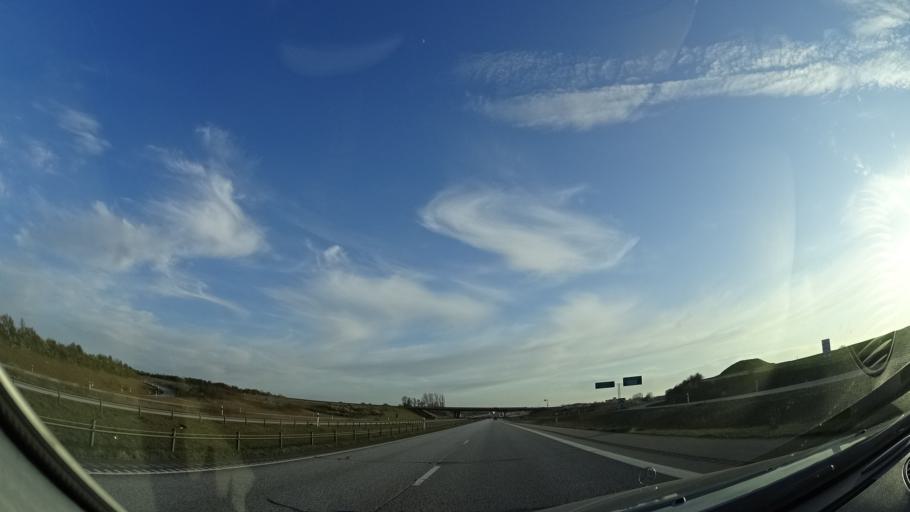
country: SE
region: Skane
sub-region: Malmo
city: Oxie
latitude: 55.5631
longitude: 13.0818
